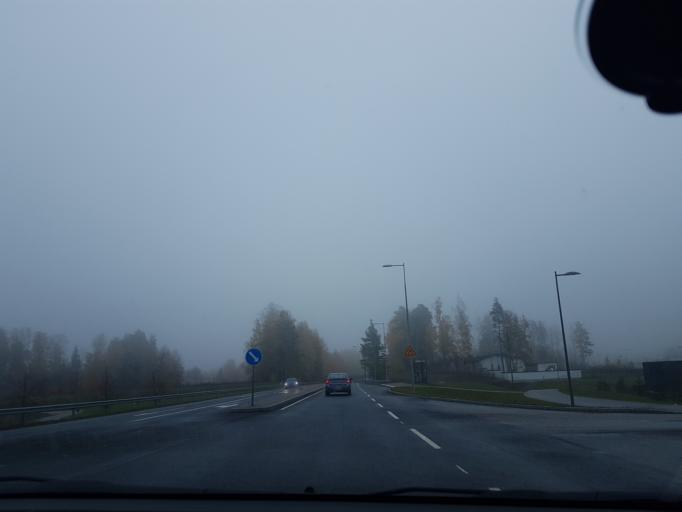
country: FI
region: Uusimaa
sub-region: Helsinki
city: Jaervenpaeae
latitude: 60.4555
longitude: 25.0953
